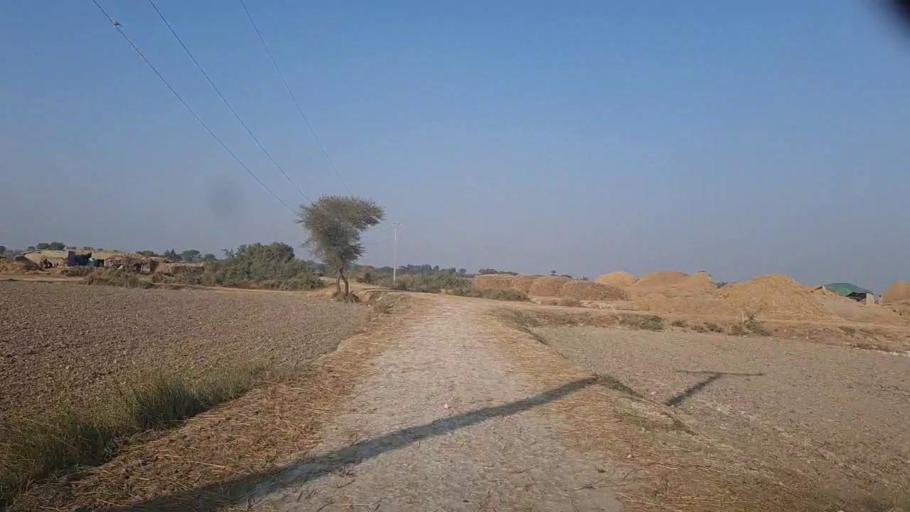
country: PK
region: Sindh
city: Thul
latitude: 28.1654
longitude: 68.8157
